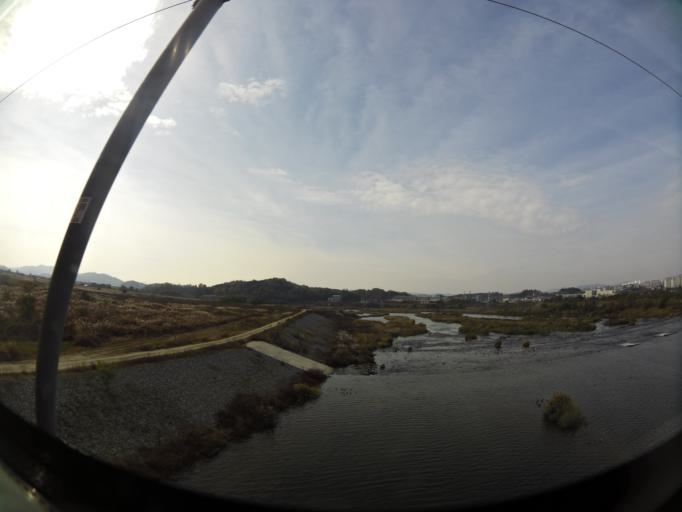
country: KR
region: Daejeon
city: Songgang-dong
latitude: 36.5819
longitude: 127.3084
